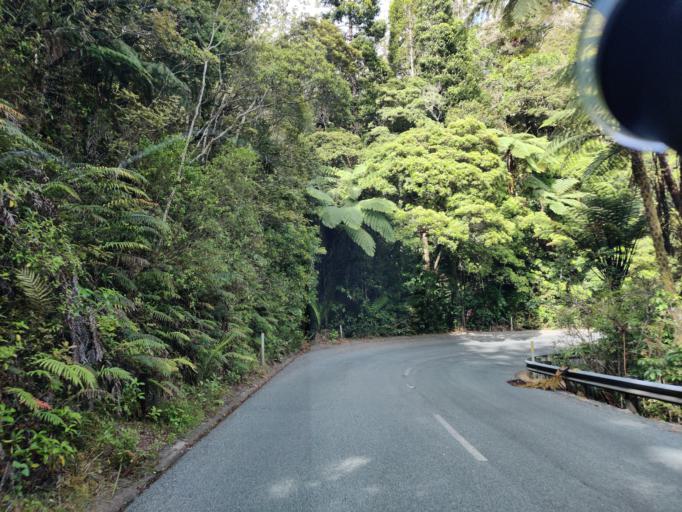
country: NZ
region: Northland
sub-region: Kaipara District
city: Dargaville
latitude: -35.6498
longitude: 173.5649
